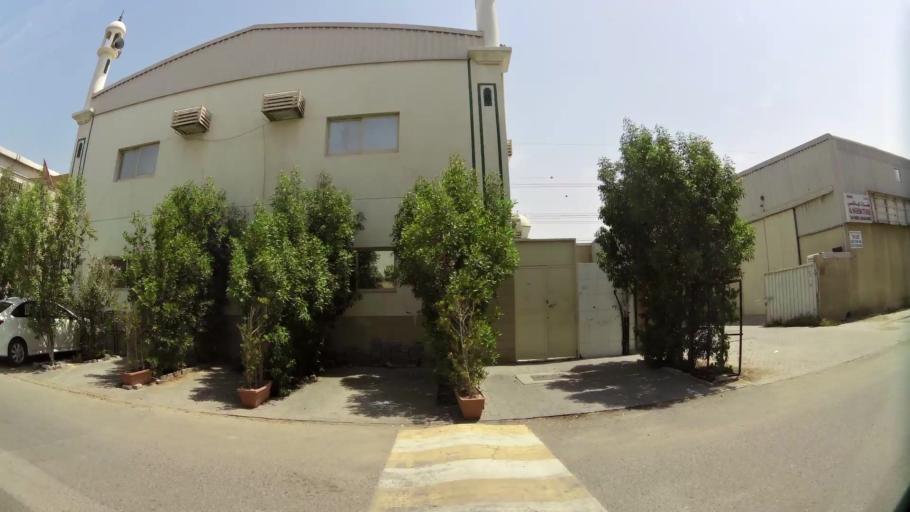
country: AE
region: Ash Shariqah
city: Sharjah
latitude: 25.2953
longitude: 55.4016
